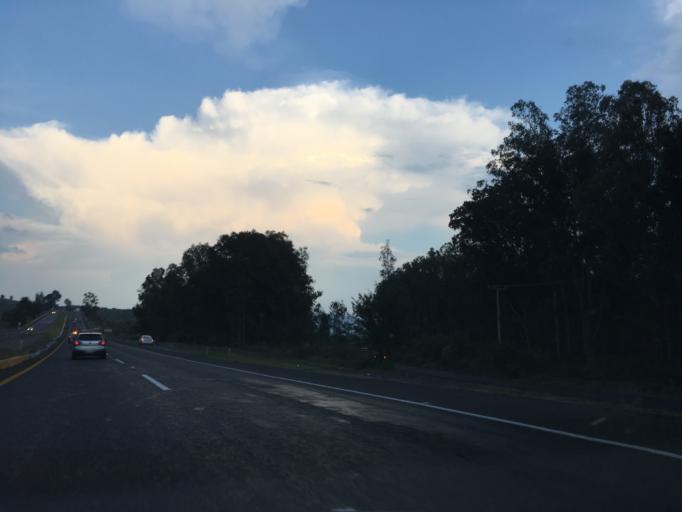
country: MX
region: Michoacan
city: Lagunillas
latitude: 19.5510
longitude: -101.3753
